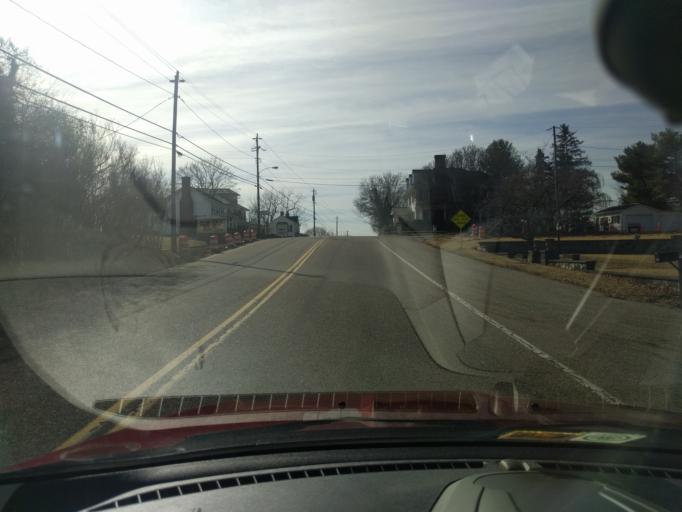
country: US
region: Virginia
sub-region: Augusta County
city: Weyers Cave
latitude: 38.2562
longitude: -78.9600
